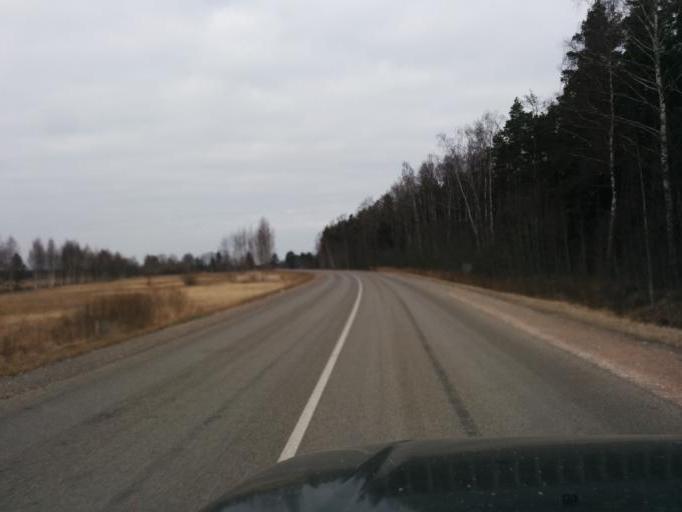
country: LV
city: Tireli
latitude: 56.8304
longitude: 23.6018
